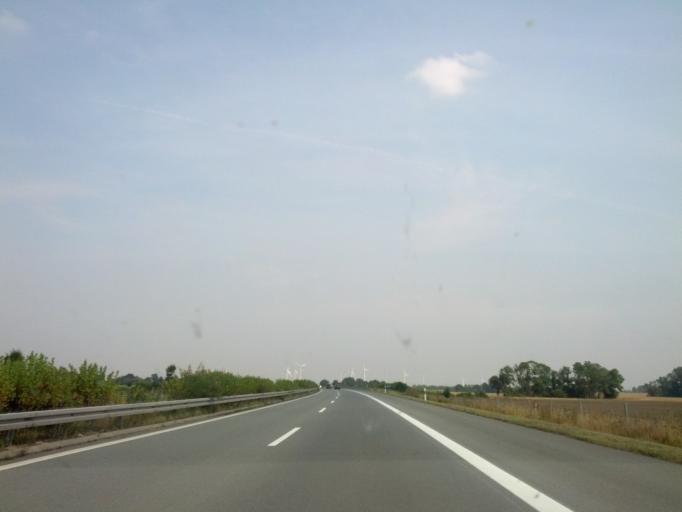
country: DE
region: Mecklenburg-Vorpommern
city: Grimmen
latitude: 54.0769
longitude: 12.9303
